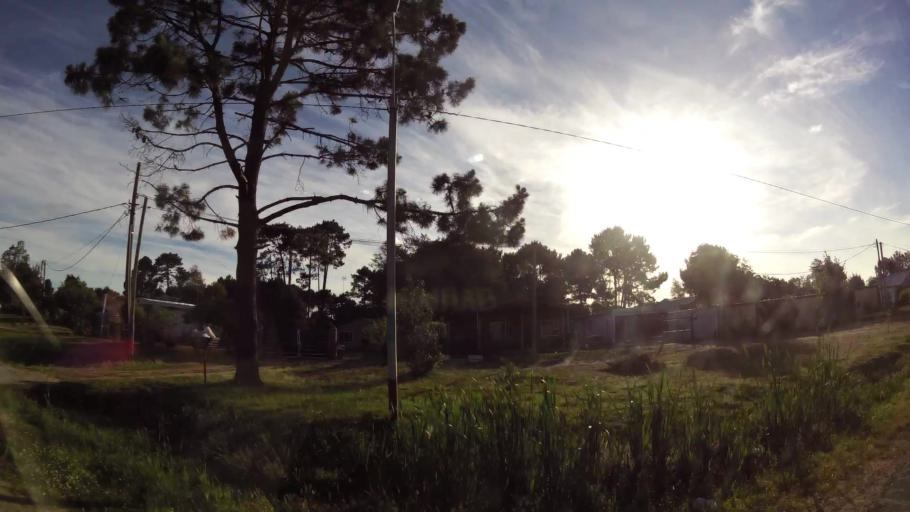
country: UY
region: Canelones
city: Empalme Olmos
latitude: -34.7700
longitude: -55.8601
